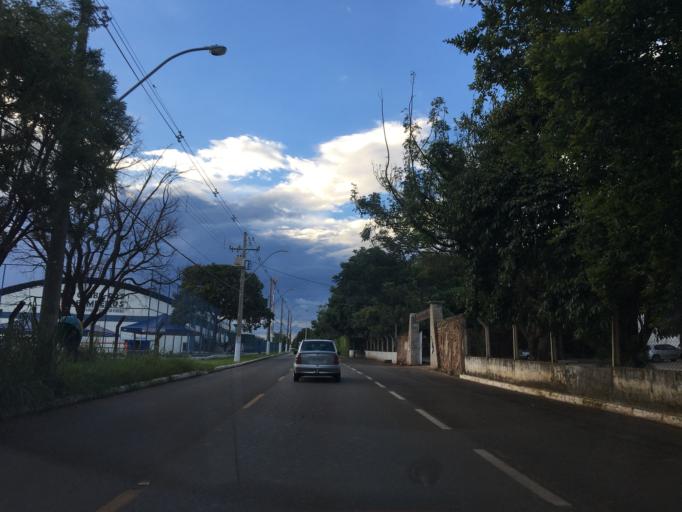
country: BR
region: Federal District
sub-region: Brasilia
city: Brasilia
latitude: -15.8179
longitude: -47.8399
